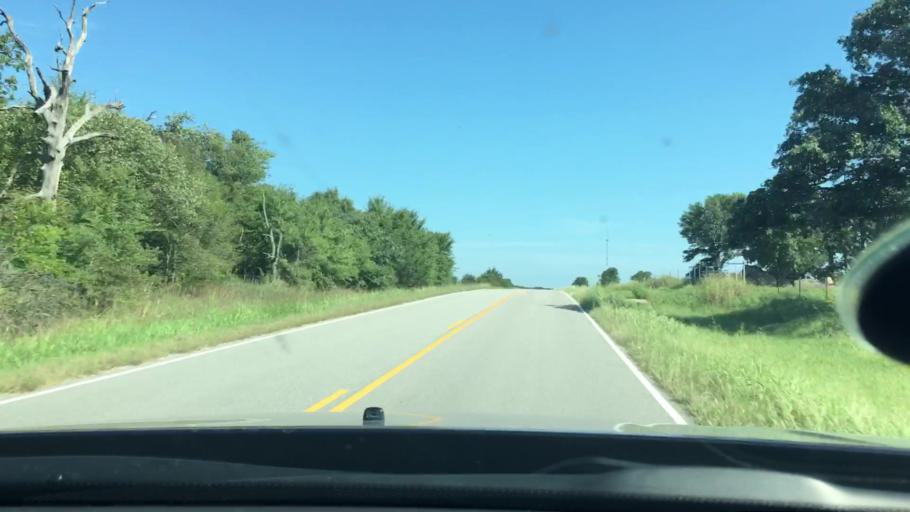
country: US
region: Oklahoma
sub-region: Johnston County
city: Tishomingo
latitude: 34.3502
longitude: -96.5488
